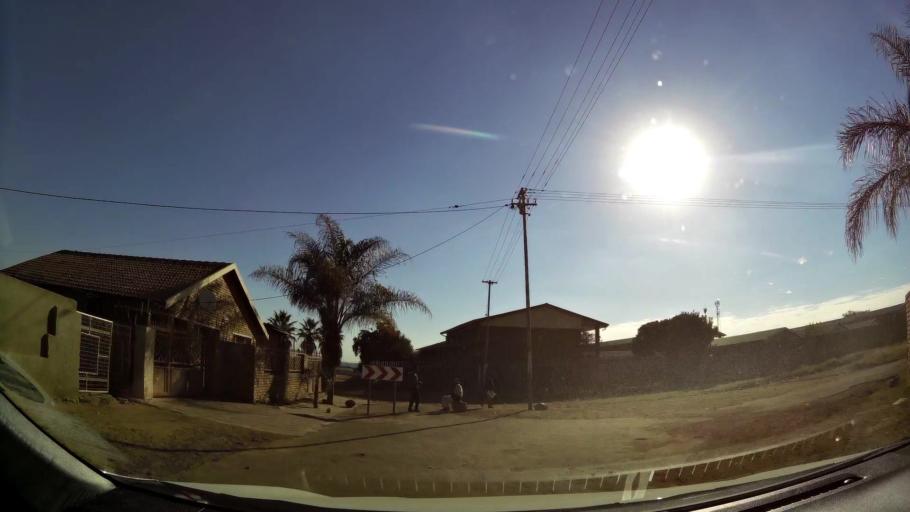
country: ZA
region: Gauteng
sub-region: City of Tshwane Metropolitan Municipality
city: Cullinan
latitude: -25.7199
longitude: 28.3866
